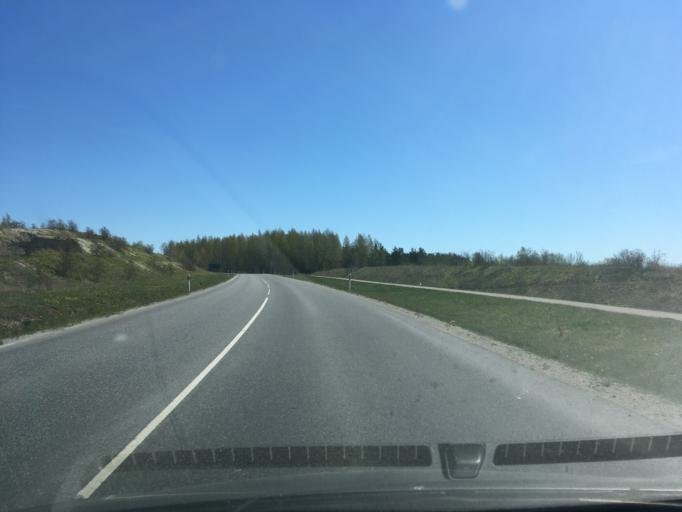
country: EE
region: Harju
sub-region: Maardu linn
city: Maardu
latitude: 59.4560
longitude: 25.0103
